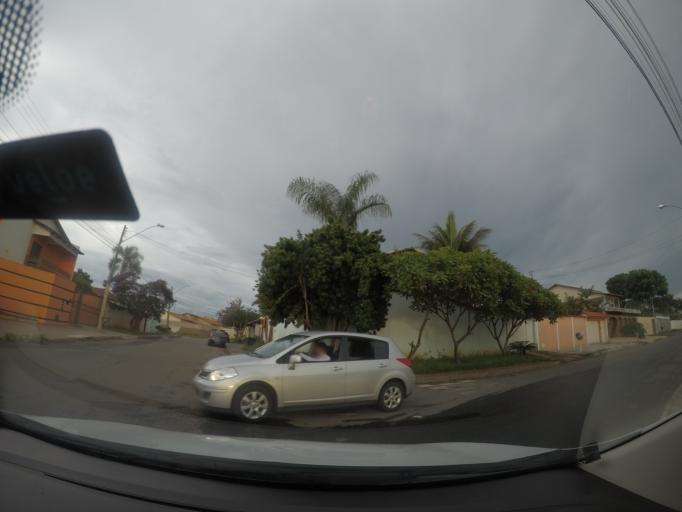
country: BR
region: Goias
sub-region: Goiania
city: Goiania
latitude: -16.7291
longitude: -49.3091
